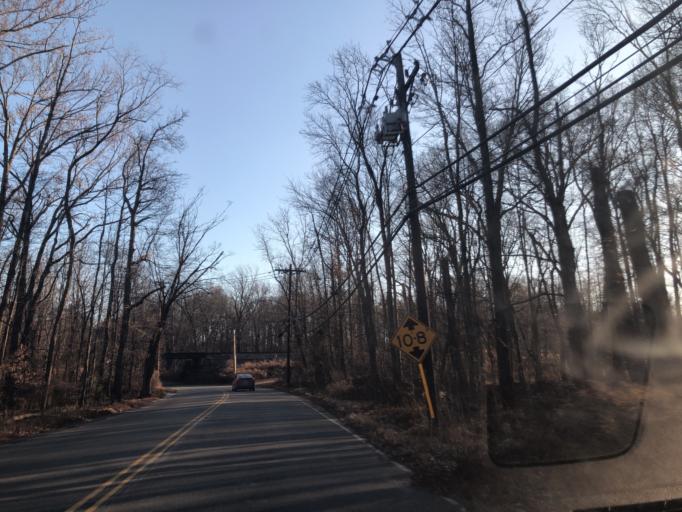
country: US
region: New Jersey
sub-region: Middlesex County
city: Iselin
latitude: 40.5564
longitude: -74.3350
